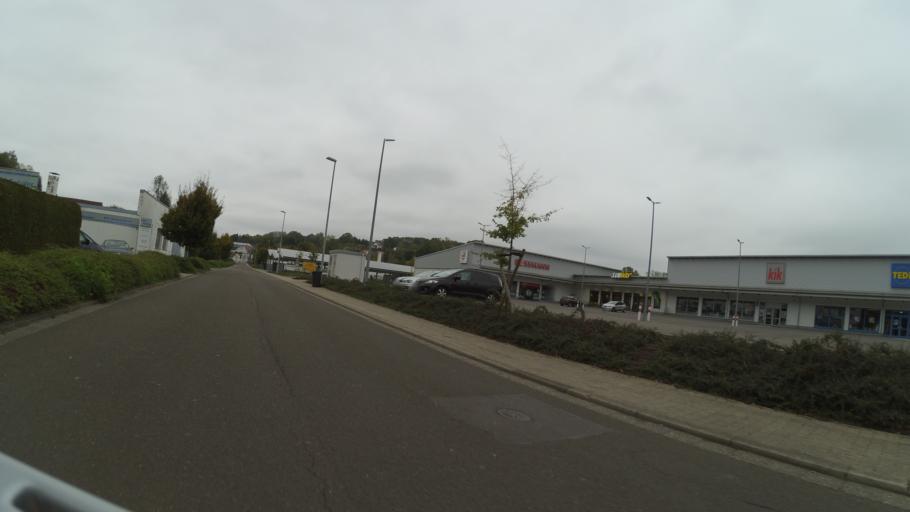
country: DE
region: Saarland
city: Blieskastel
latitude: 49.2464
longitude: 7.2596
